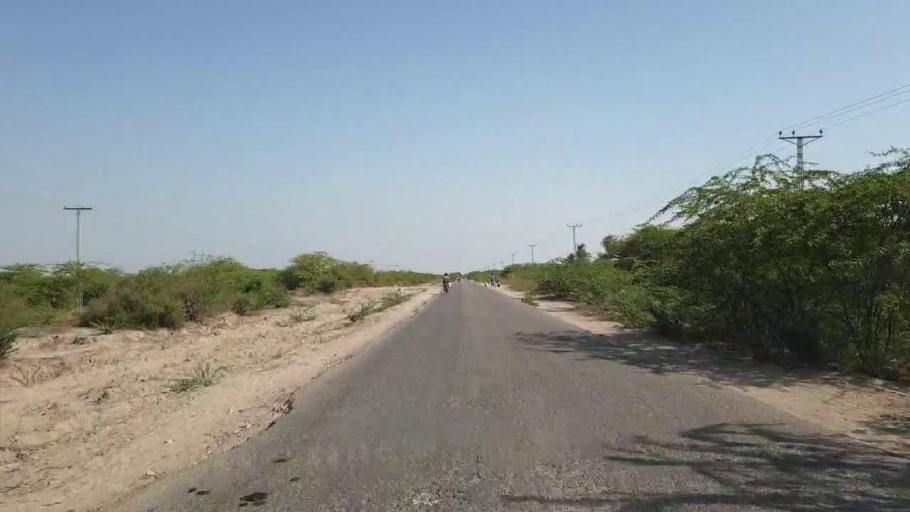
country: PK
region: Sindh
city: Chor
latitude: 25.4643
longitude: 69.7658
